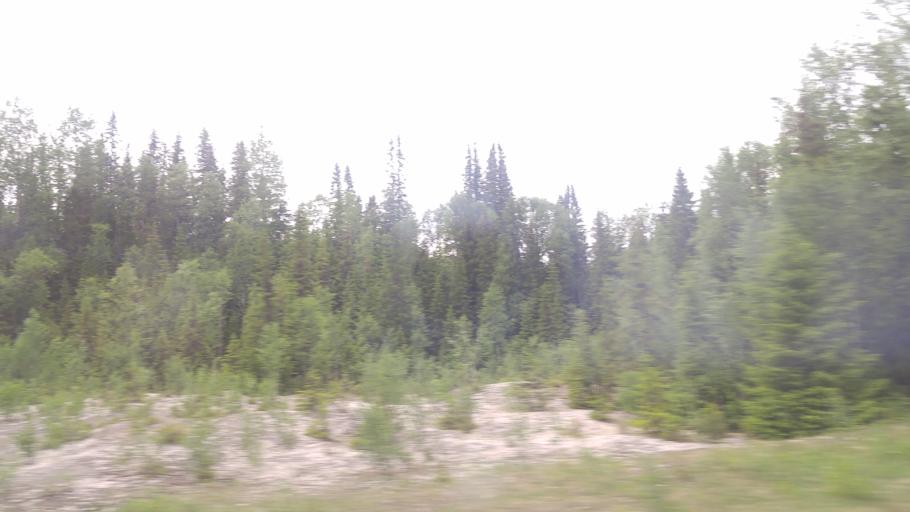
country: SE
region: Jaemtland
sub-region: Are Kommun
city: Are
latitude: 63.3732
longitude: 12.7259
